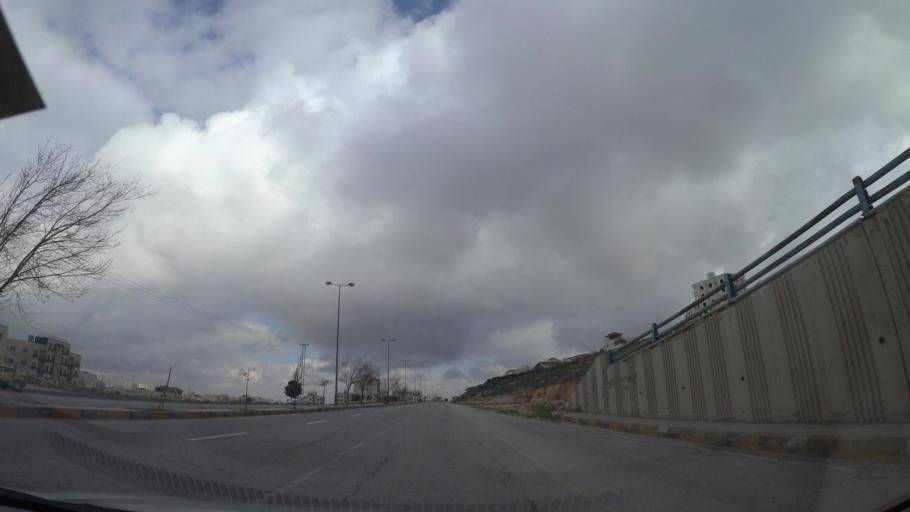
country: JO
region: Amman
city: Al Jubayhah
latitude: 32.0391
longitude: 35.8863
